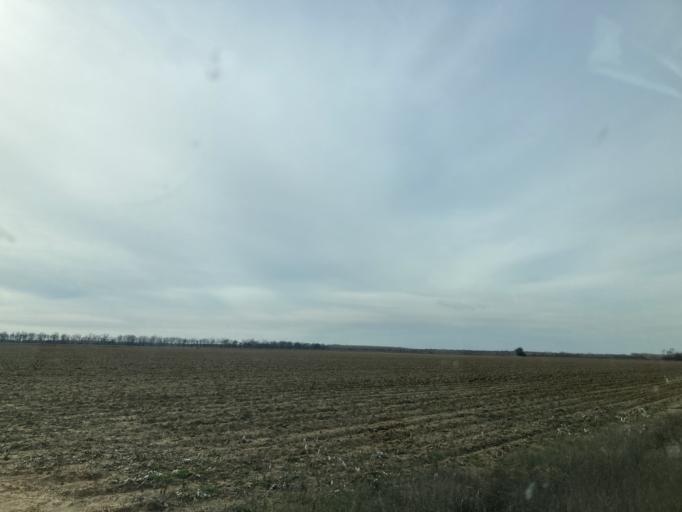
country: US
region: Mississippi
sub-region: Humphreys County
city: Belzoni
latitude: 33.1237
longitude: -90.6196
